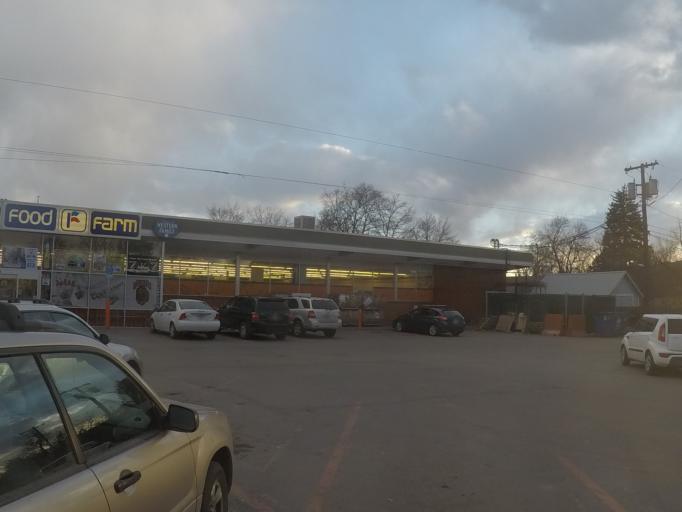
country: US
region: Montana
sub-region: Missoula County
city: Missoula
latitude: 46.8648
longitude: -114.0040
